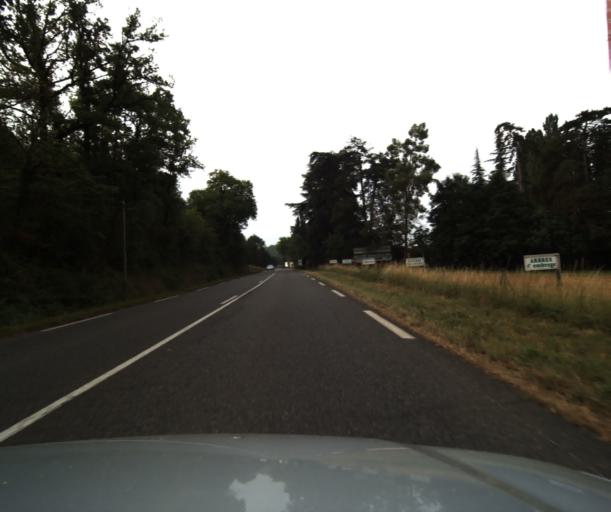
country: FR
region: Midi-Pyrenees
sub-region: Departement du Gers
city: Mirande
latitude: 43.5241
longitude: 0.4170
